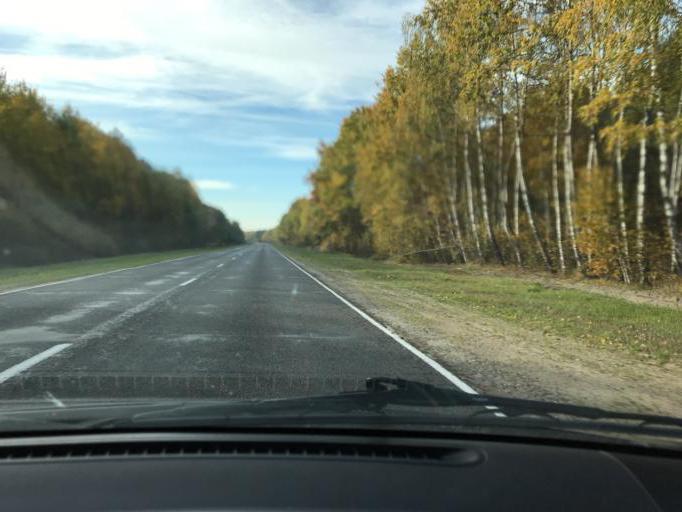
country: BY
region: Brest
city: Ivanava
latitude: 52.1566
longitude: 25.7698
